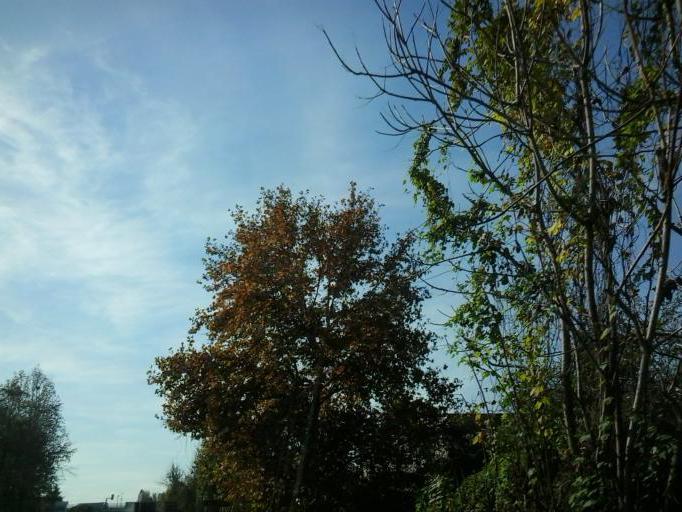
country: IT
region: Lombardy
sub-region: Provincia di Brescia
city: Capriano del Colle
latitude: 45.4825
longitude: 10.1447
